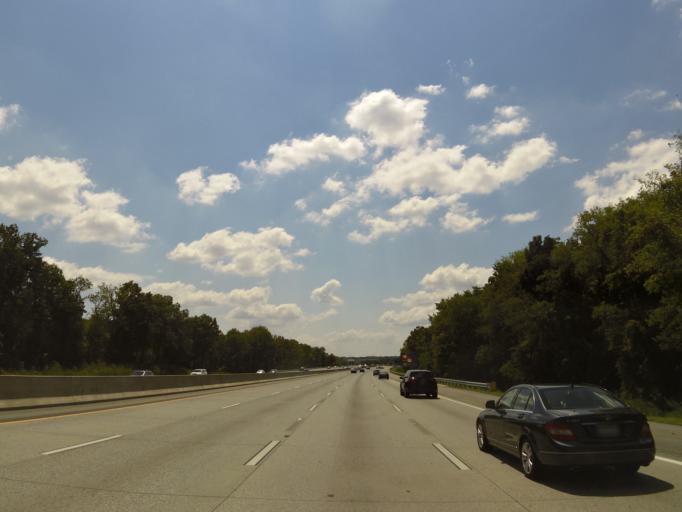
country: US
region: North Carolina
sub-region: Cabarrus County
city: Harrisburg
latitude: 35.3789
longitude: -80.7071
